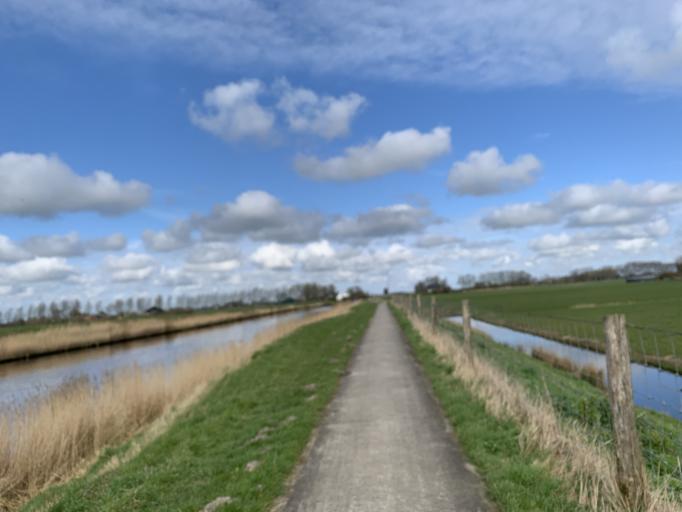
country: NL
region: Groningen
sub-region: Gemeente Zuidhorn
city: Aduard
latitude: 53.2656
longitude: 6.5074
